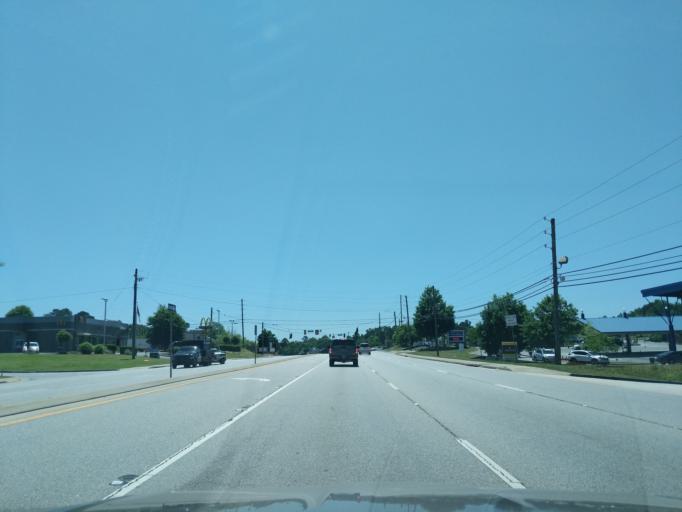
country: US
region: Georgia
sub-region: Columbia County
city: Martinez
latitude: 33.5294
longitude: -82.0744
